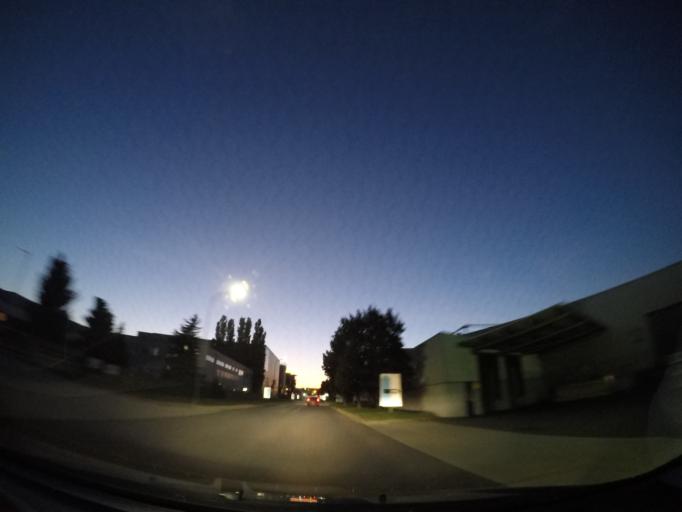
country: AT
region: Lower Austria
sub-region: Politischer Bezirk Modling
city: Biedermannsdorf
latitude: 48.0750
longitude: 16.3334
